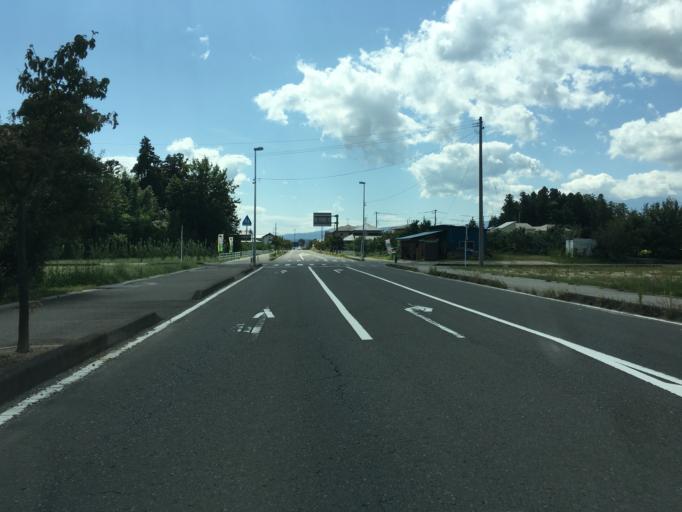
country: JP
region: Fukushima
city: Fukushima-shi
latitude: 37.7895
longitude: 140.4277
